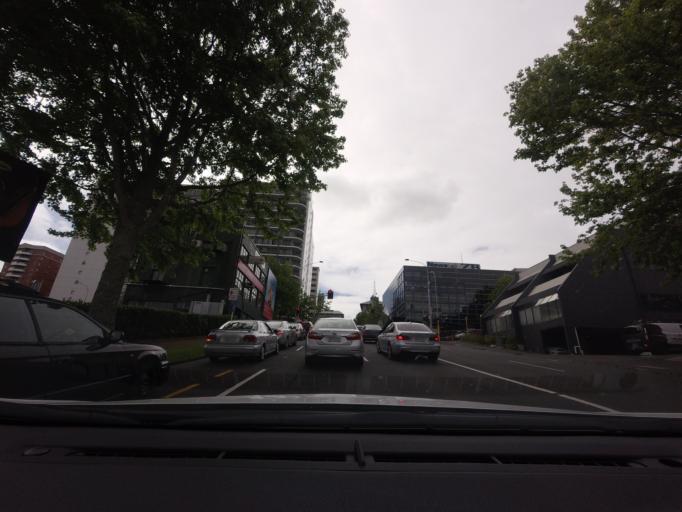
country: NZ
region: Auckland
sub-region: Auckland
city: Auckland
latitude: -36.8511
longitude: 174.7579
